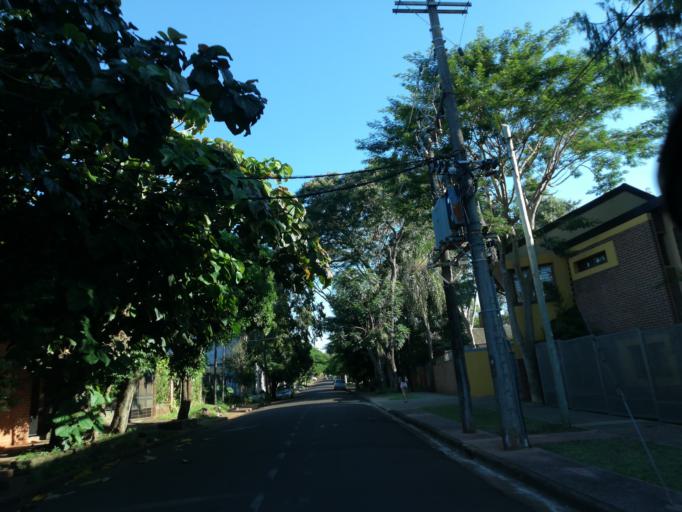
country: AR
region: Misiones
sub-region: Departamento de Capital
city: Posadas
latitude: -27.3558
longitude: -55.9207
